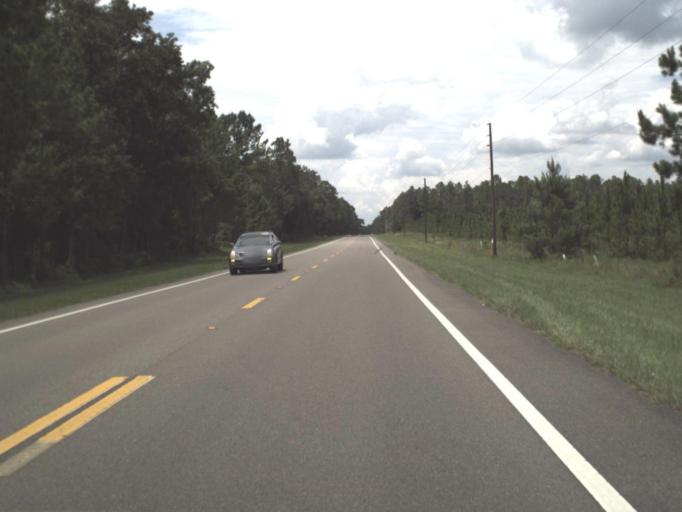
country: US
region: Florida
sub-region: Alachua County
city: Archer
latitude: 29.4734
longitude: -82.4840
